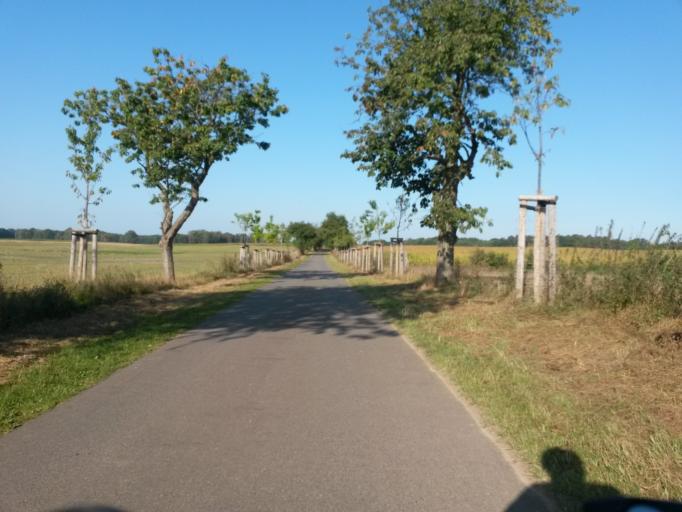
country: DE
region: Brandenburg
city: Templin
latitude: 53.1309
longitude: 13.4625
